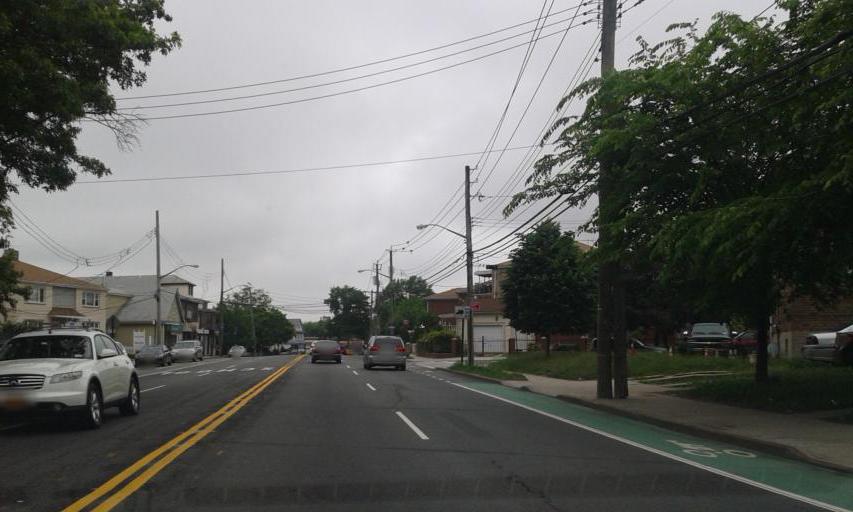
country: US
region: New Jersey
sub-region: Hudson County
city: Bayonne
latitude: 40.6135
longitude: -74.1005
